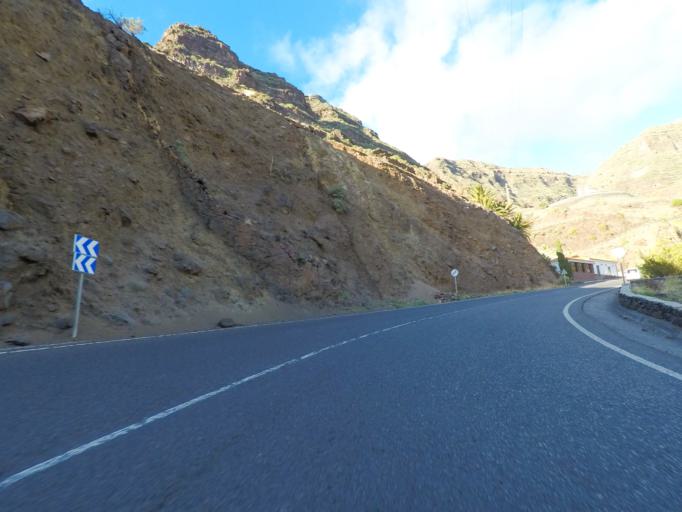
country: ES
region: Canary Islands
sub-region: Provincia de Santa Cruz de Tenerife
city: Vallehermosa
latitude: 28.1151
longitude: -17.3150
